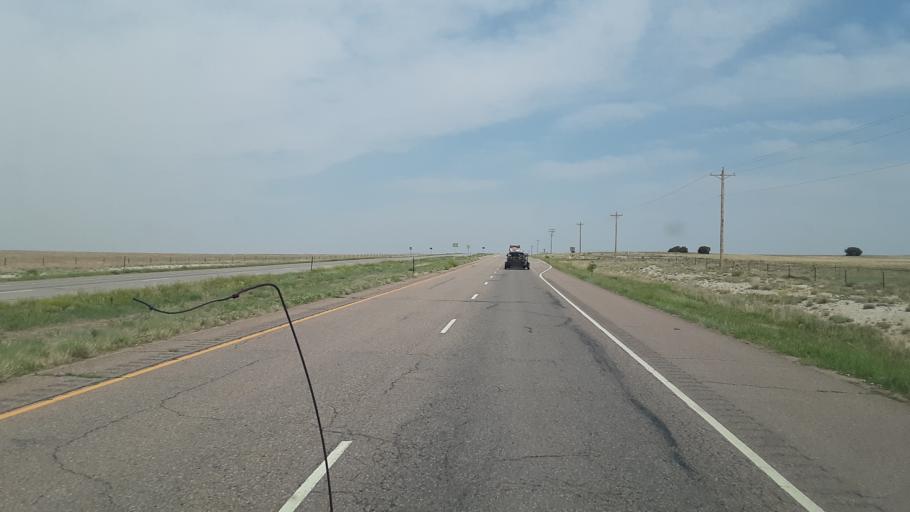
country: US
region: Colorado
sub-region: Fremont County
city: Penrose
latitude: 38.3715
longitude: -104.9383
